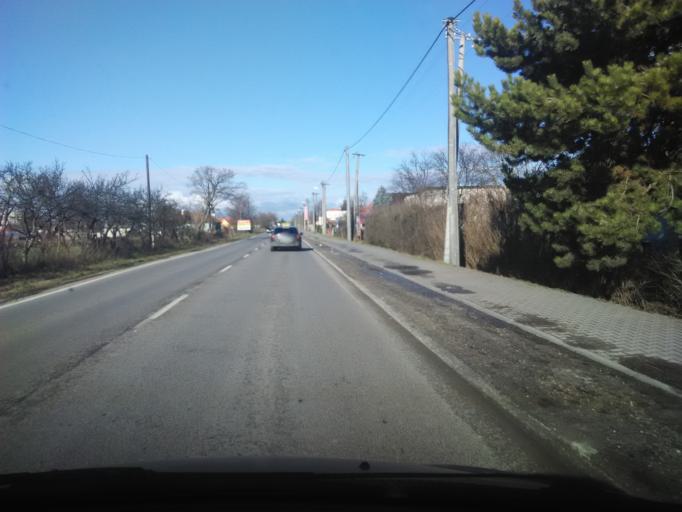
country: SK
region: Nitriansky
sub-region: Okres Nitra
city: Nitra
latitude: 48.2309
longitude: 18.1306
